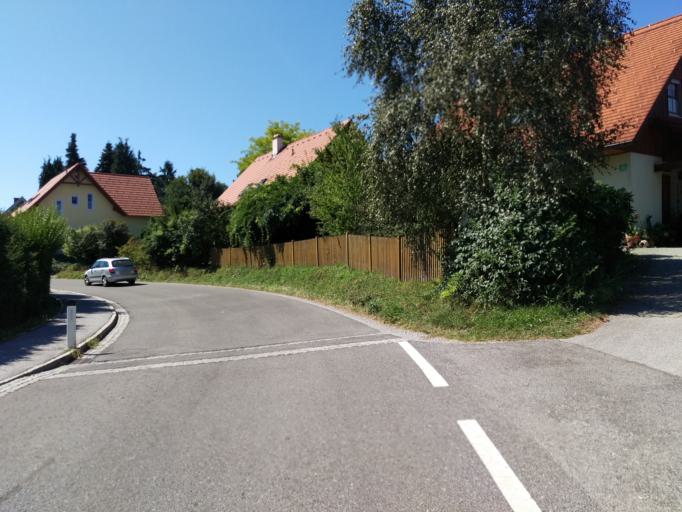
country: AT
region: Styria
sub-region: Politischer Bezirk Graz-Umgebung
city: Eggersdorf bei Graz
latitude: 47.0892
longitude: 15.5607
